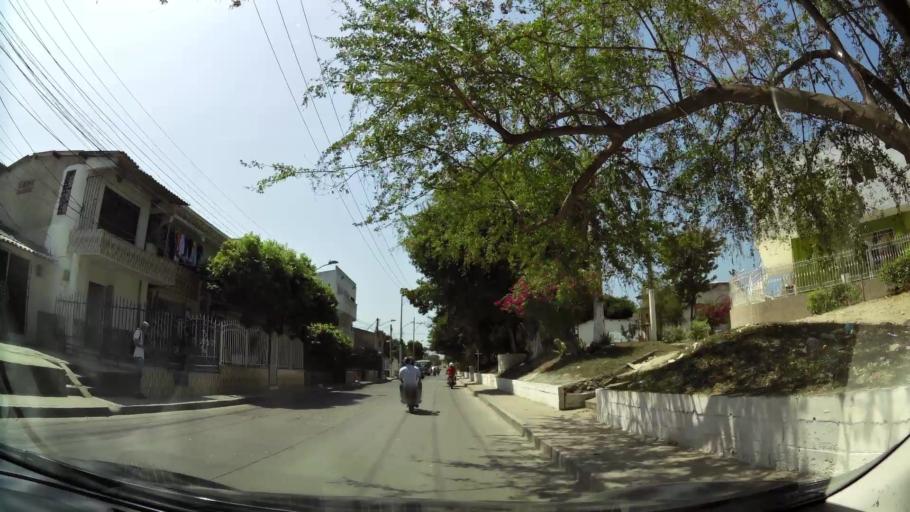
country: CO
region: Bolivar
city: Cartagena
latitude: 10.4021
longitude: -75.4875
